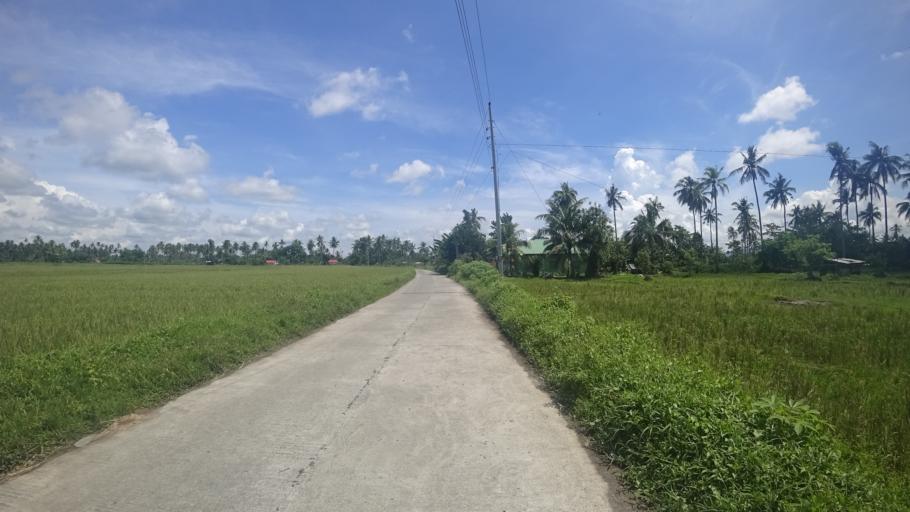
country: PH
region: Eastern Visayas
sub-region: Province of Leyte
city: Alangalang
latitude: 11.2285
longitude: 124.8456
